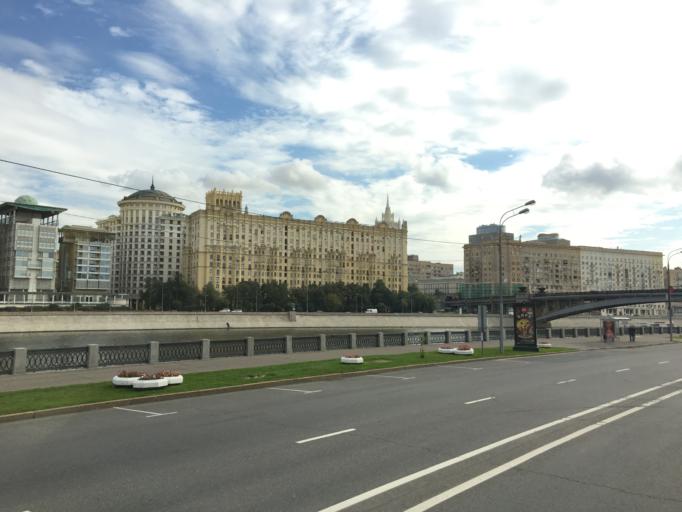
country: RU
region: Moskovskaya
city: Dorogomilovo
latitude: 55.7503
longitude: 37.5720
